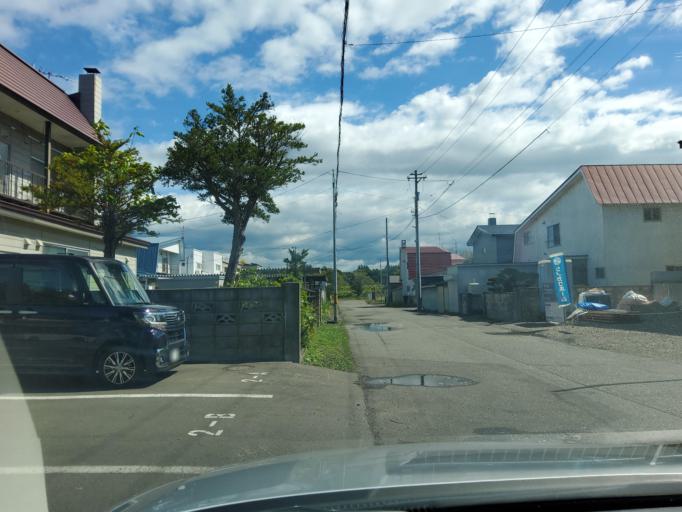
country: JP
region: Hokkaido
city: Otofuke
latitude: 42.9669
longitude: 143.2138
